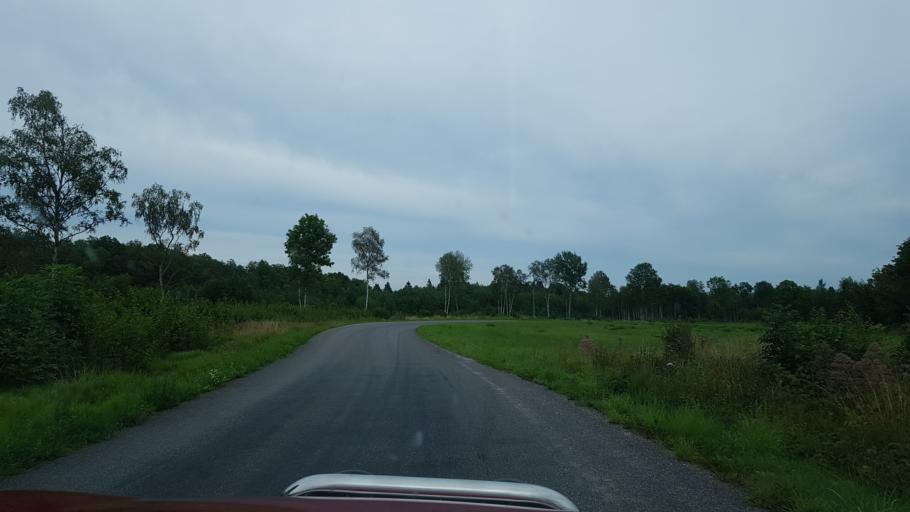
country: EE
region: Laeaene
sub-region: Lihula vald
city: Lihula
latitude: 58.8327
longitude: 23.8144
